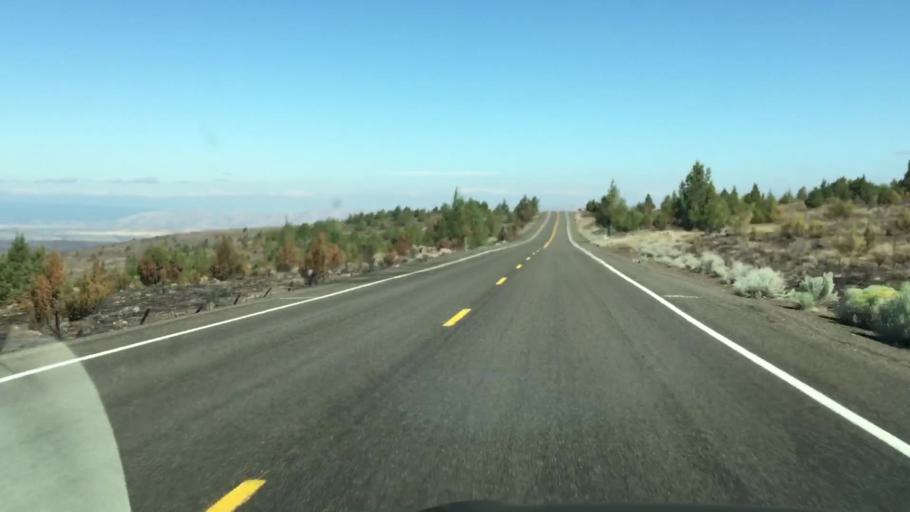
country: US
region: Oregon
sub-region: Jefferson County
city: Warm Springs
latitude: 45.0801
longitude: -121.0249
